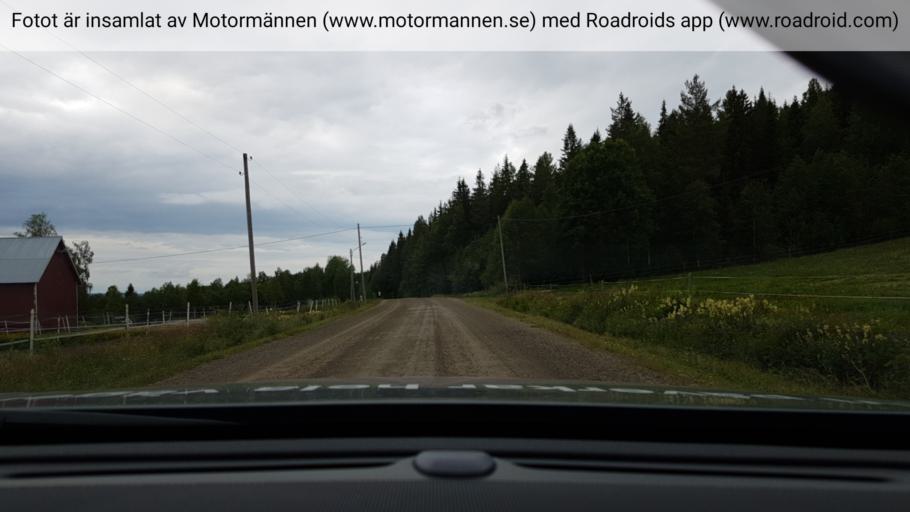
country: SE
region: Vaesterbotten
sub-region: Vannas Kommun
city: Vannasby
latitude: 64.0942
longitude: 20.0183
